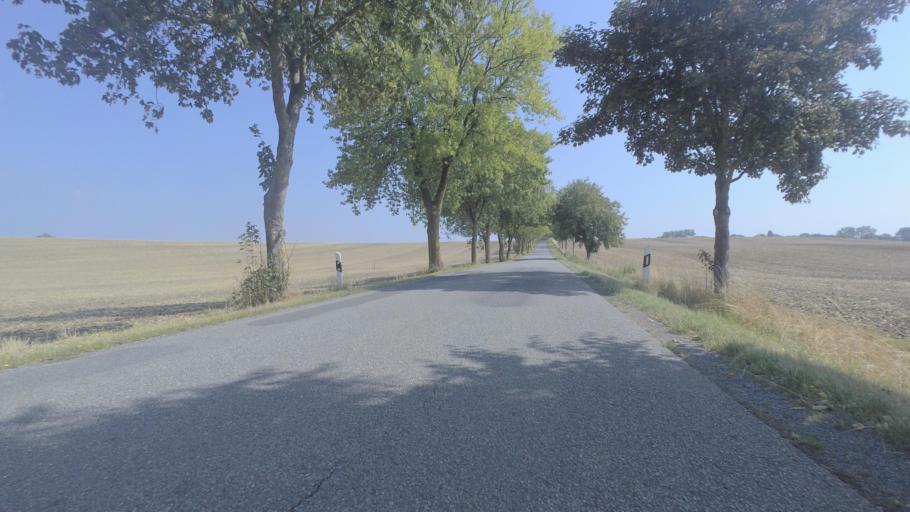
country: DE
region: Mecklenburg-Vorpommern
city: Pampow
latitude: 53.6879
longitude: 12.5891
